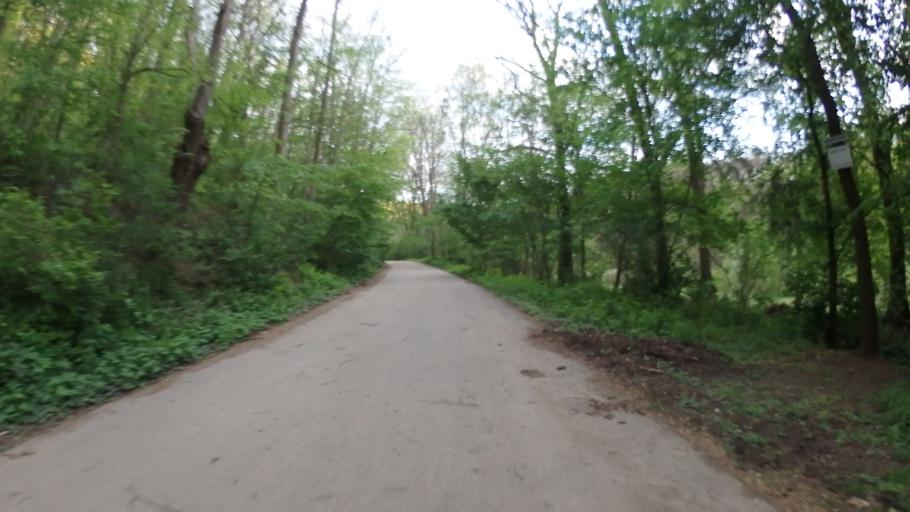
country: CZ
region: South Moravian
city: Strelice
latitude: 49.1418
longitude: 16.4767
